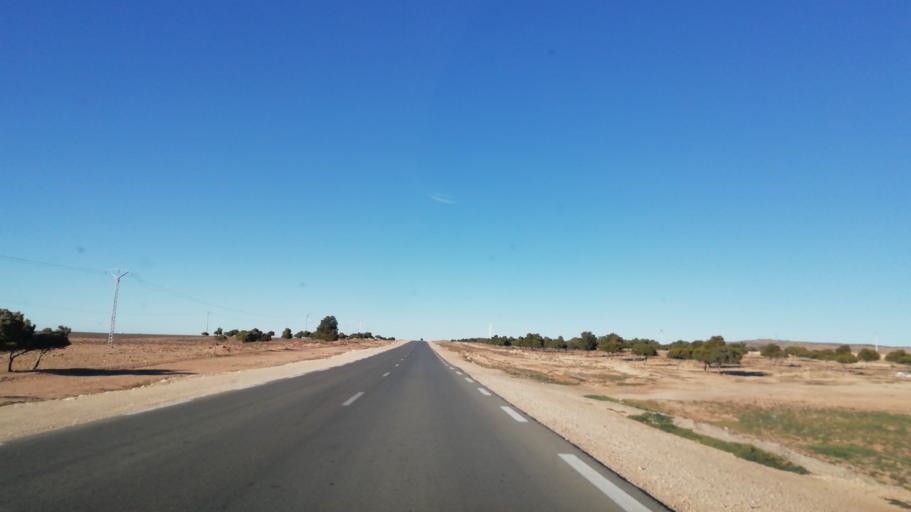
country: DZ
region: Tlemcen
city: Sebdou
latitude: 34.2403
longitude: -1.2568
